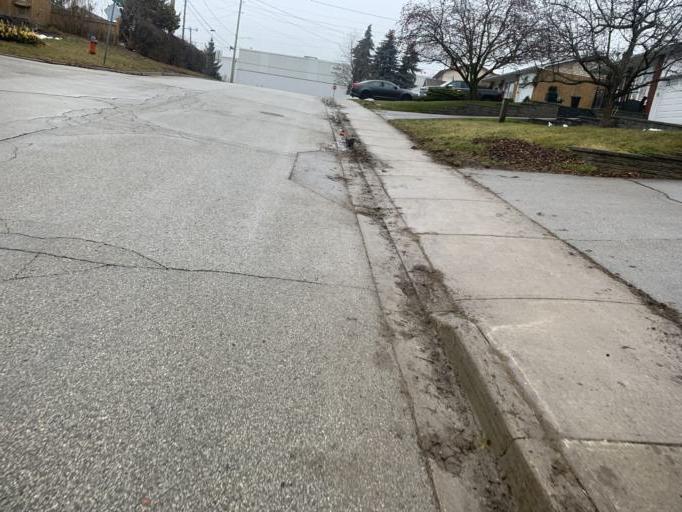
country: CA
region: Ontario
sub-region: Halton
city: Milton
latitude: 43.6573
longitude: -79.9259
